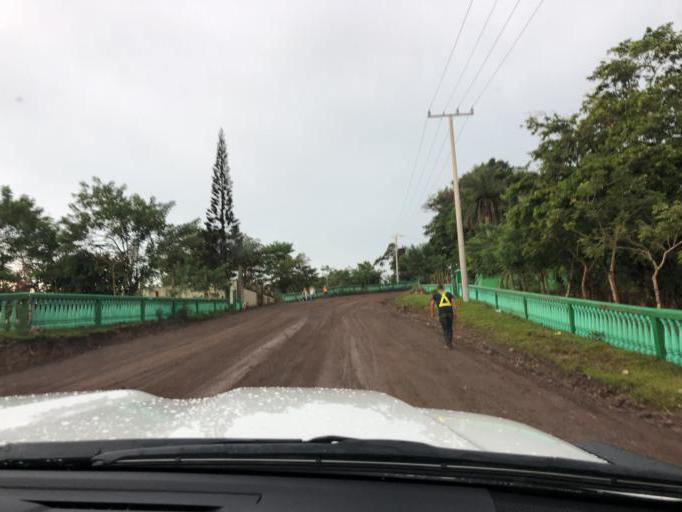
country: NI
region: Chontales
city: La Libertad
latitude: 12.2051
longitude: -85.1709
